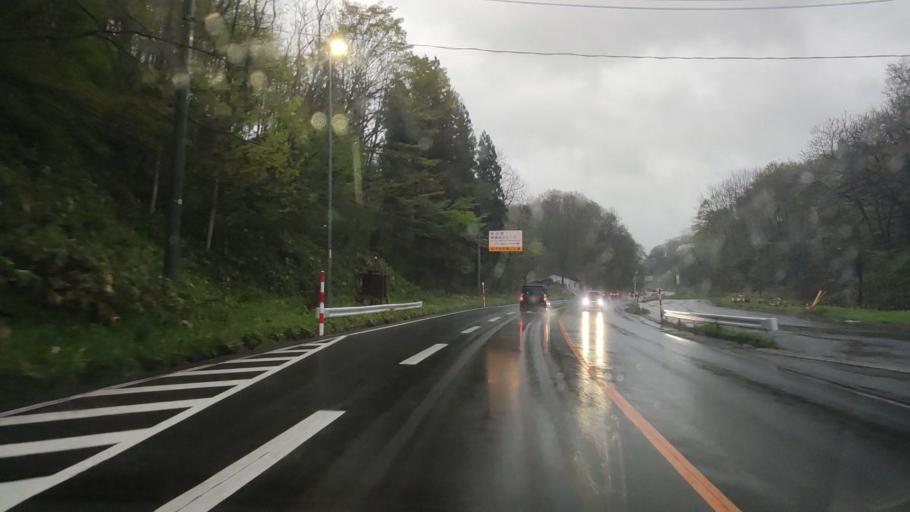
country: JP
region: Akita
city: Akita
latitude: 39.6450
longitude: 140.2888
